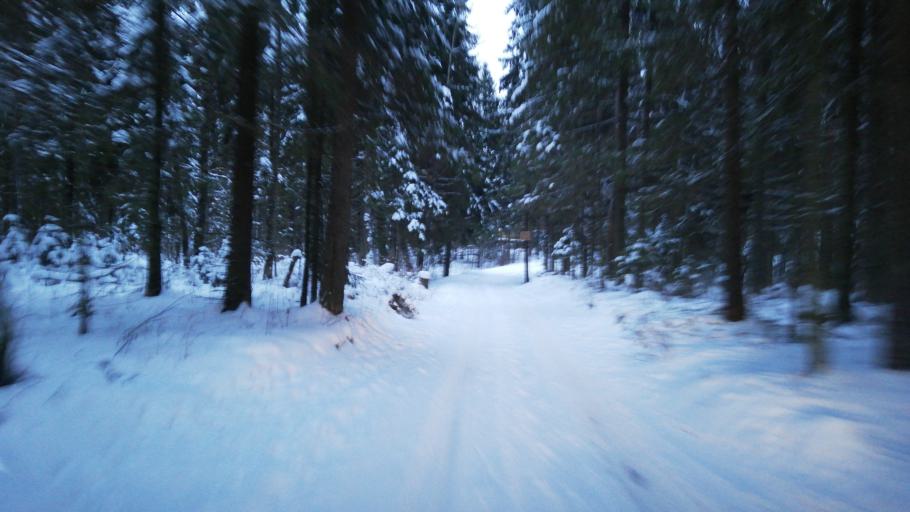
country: RU
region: Jaroslavl
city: Krasnyye Tkachi
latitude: 57.4469
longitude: 39.7985
